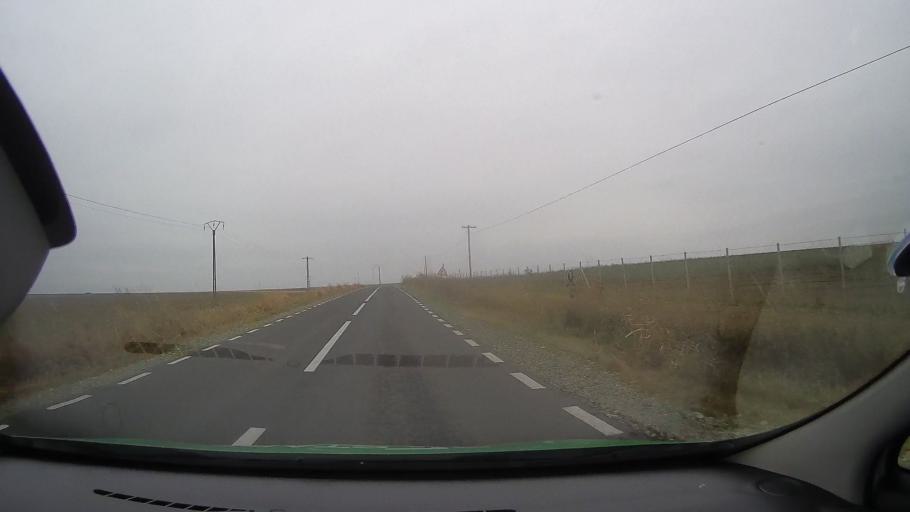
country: RO
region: Constanta
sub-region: Comuna Tortoman
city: Tortoman
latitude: 44.3557
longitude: 28.2126
